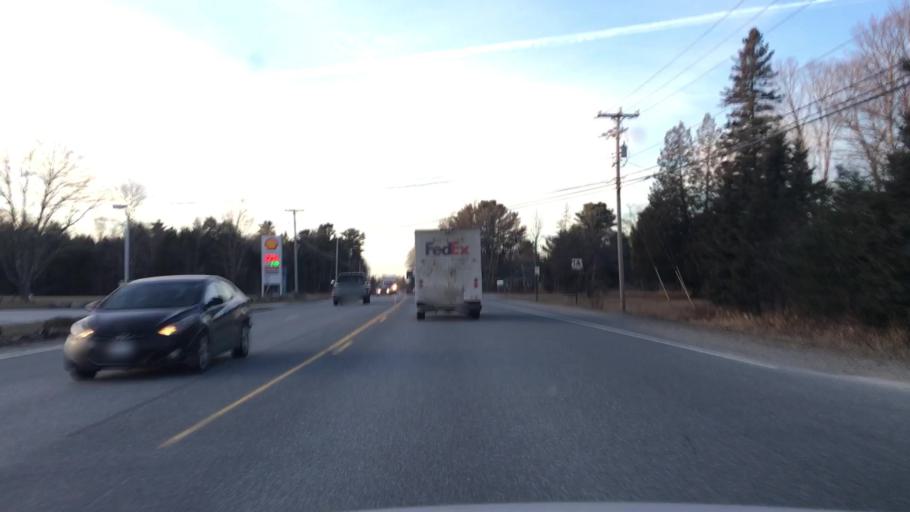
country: US
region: Maine
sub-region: Penobscot County
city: Holden
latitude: 44.7497
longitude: -68.6492
